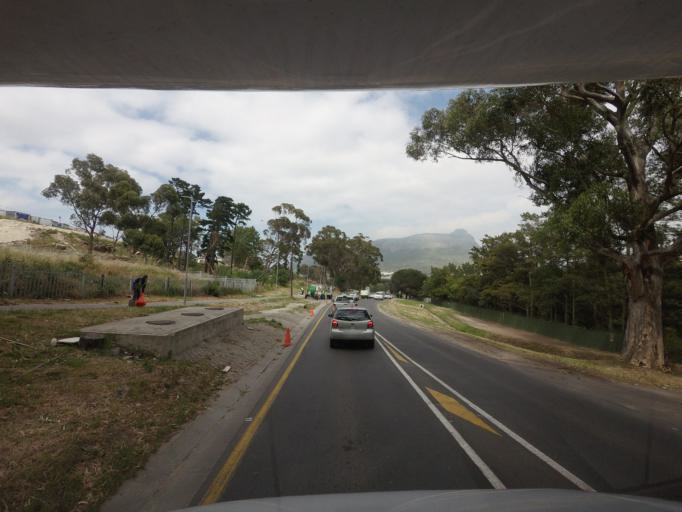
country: ZA
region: Western Cape
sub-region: City of Cape Town
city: Constantia
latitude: -34.0246
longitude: 18.3615
